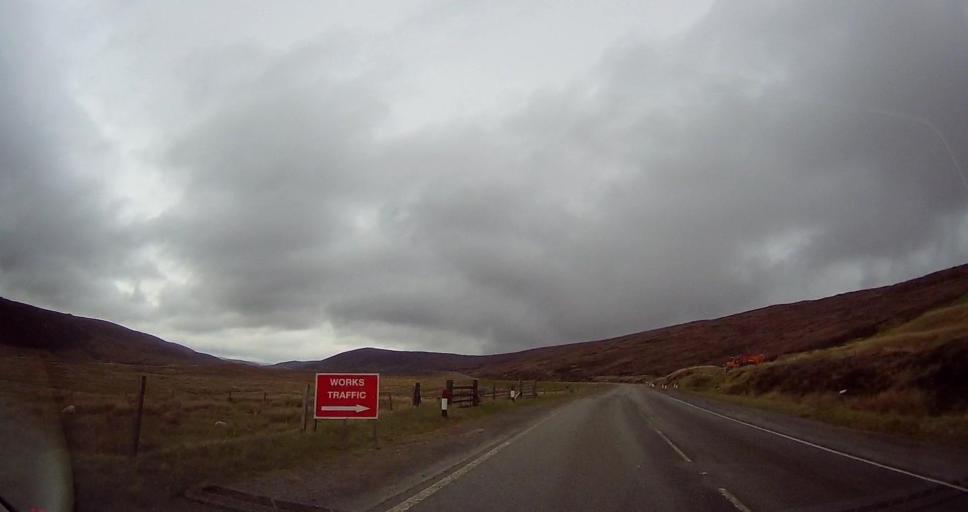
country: GB
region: Scotland
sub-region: Shetland Islands
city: Lerwick
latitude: 60.2841
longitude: -1.2436
